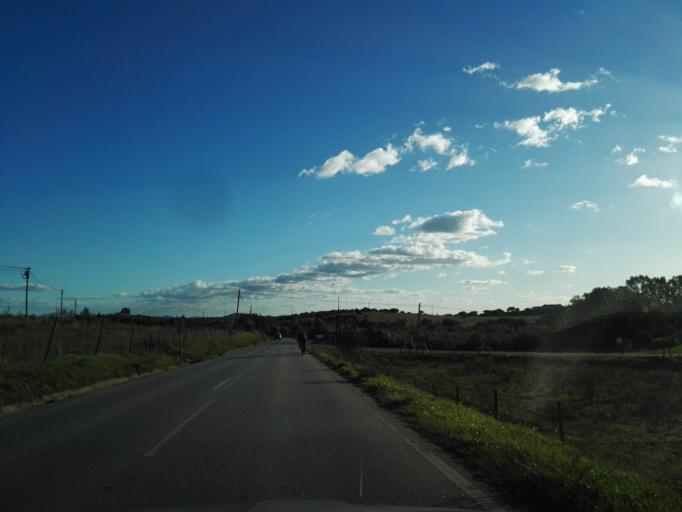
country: PT
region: Portalegre
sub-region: Elvas
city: Elvas
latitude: 38.9034
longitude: -7.1792
